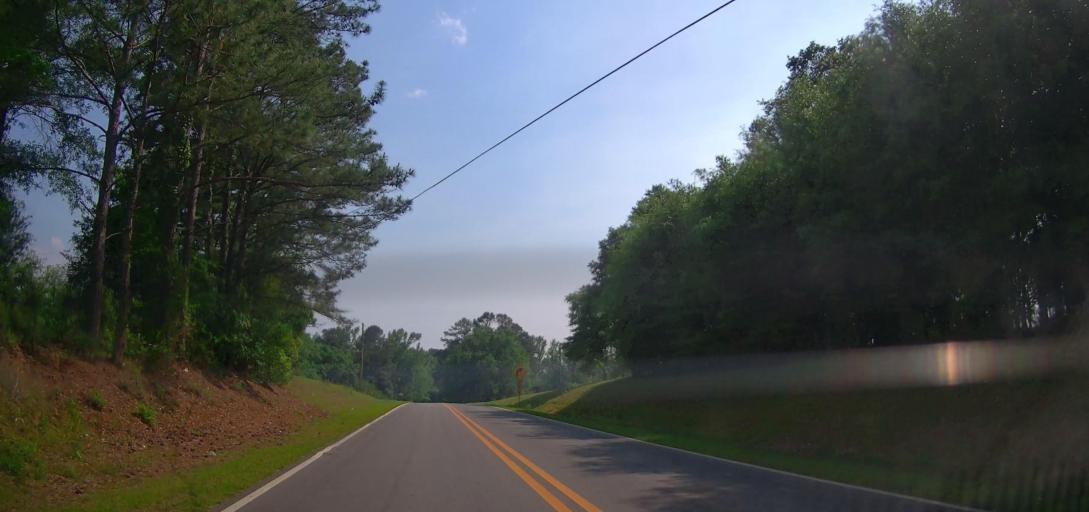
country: US
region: Georgia
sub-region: Laurens County
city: East Dublin
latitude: 32.5678
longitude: -82.8652
